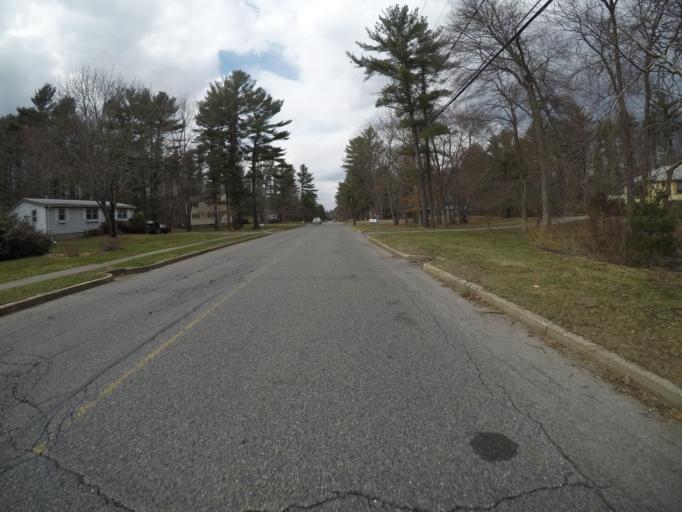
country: US
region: Massachusetts
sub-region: Bristol County
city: Easton
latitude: 42.0409
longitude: -71.1140
